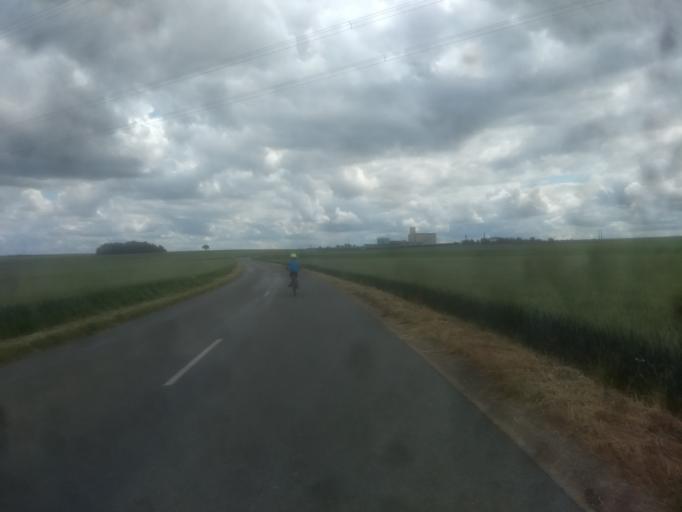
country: FR
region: Nord-Pas-de-Calais
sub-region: Departement du Pas-de-Calais
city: Agny
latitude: 50.2235
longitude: 2.7475
